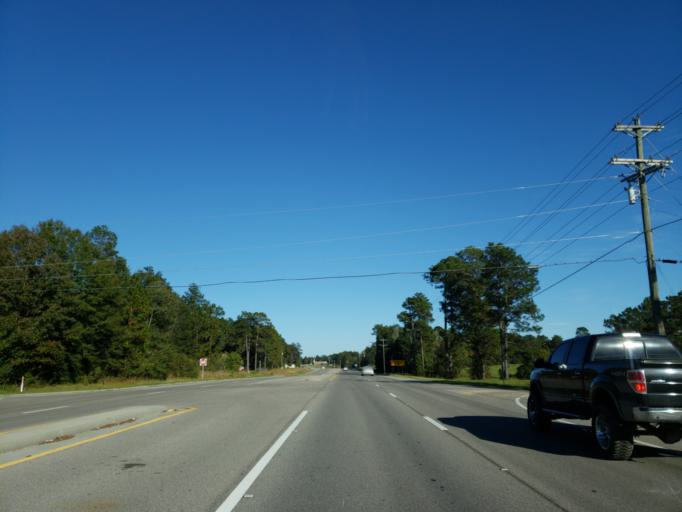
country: US
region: Mississippi
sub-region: Forrest County
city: Petal
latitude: 31.3509
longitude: -89.1854
